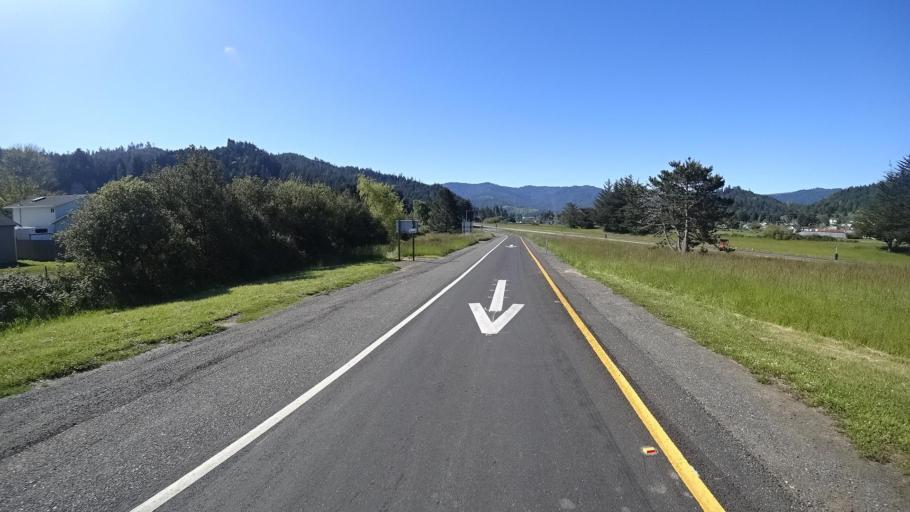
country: US
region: California
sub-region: Humboldt County
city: Rio Dell
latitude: 40.4990
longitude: -124.0981
